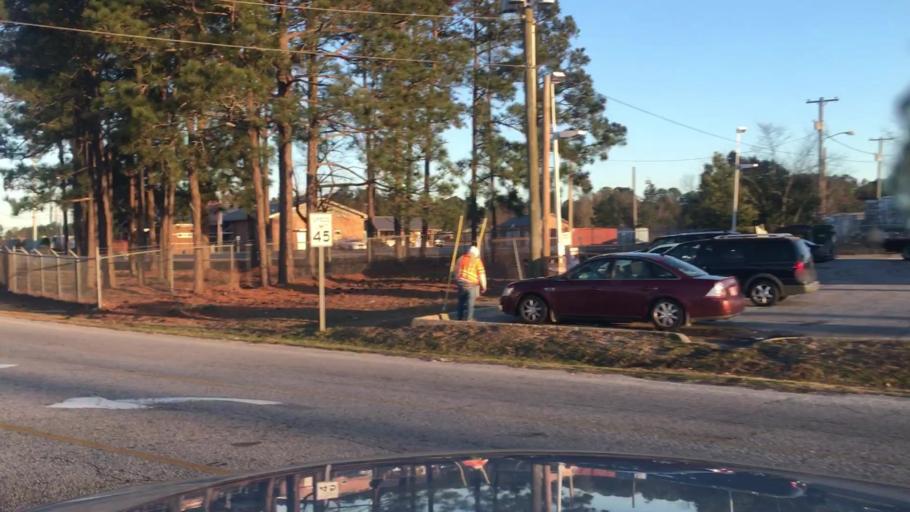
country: US
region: North Carolina
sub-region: Cumberland County
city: Hope Mills
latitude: 34.9968
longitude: -78.9020
